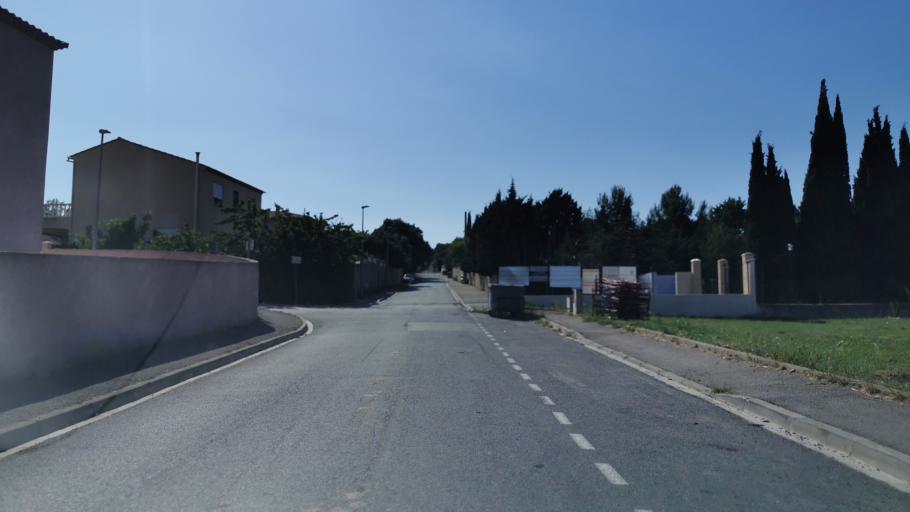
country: FR
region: Languedoc-Roussillon
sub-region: Departement de l'Aude
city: Narbonne
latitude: 43.1424
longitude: 2.9707
